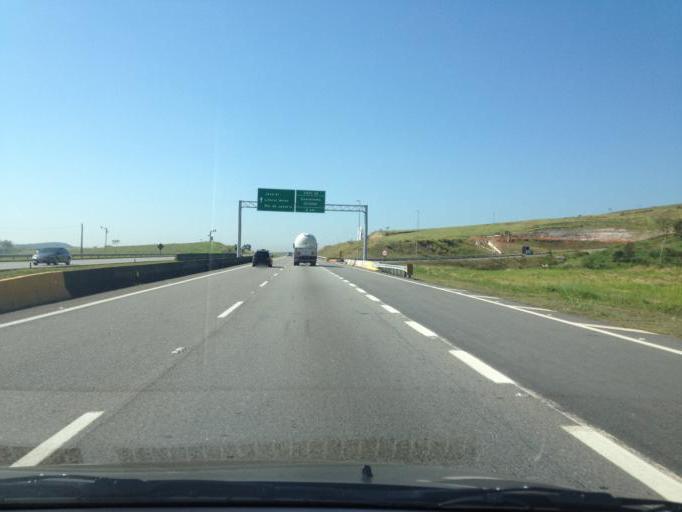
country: BR
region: Sao Paulo
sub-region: Guararema
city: Guararema
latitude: -23.3601
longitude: -46.0786
